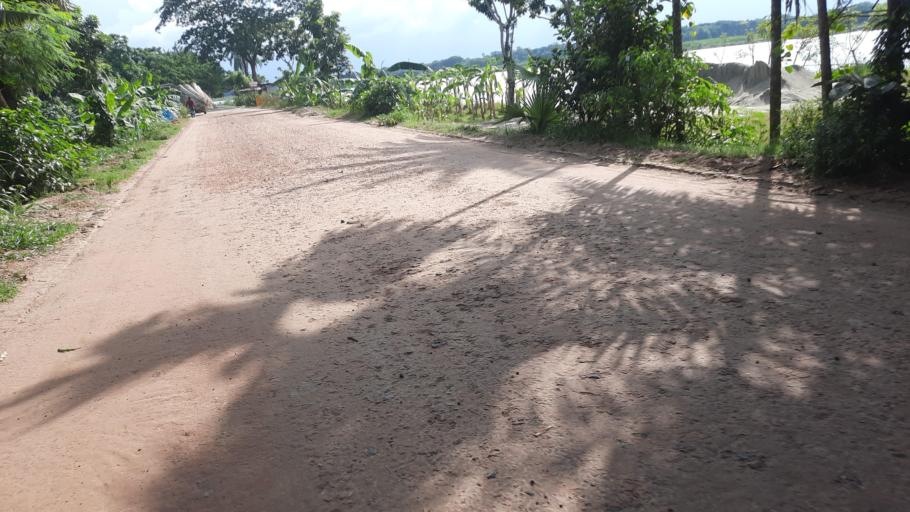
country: BD
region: Khulna
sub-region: Magura
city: Magura
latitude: 23.4612
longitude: 89.6107
